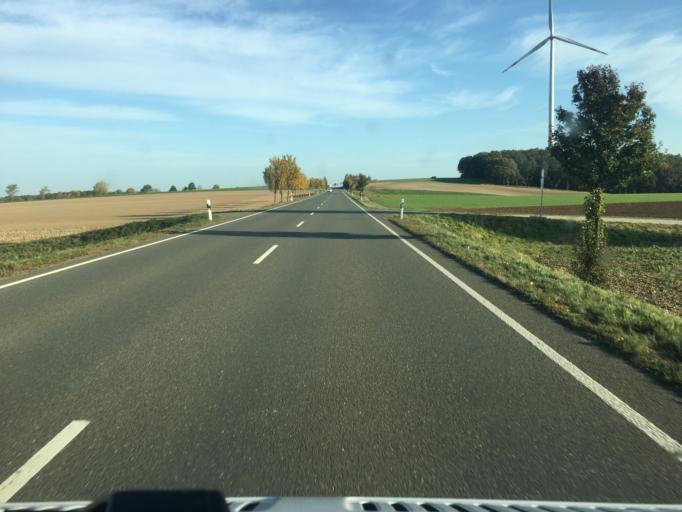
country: DE
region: Thuringia
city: Thonhausen
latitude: 50.8286
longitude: 12.3384
